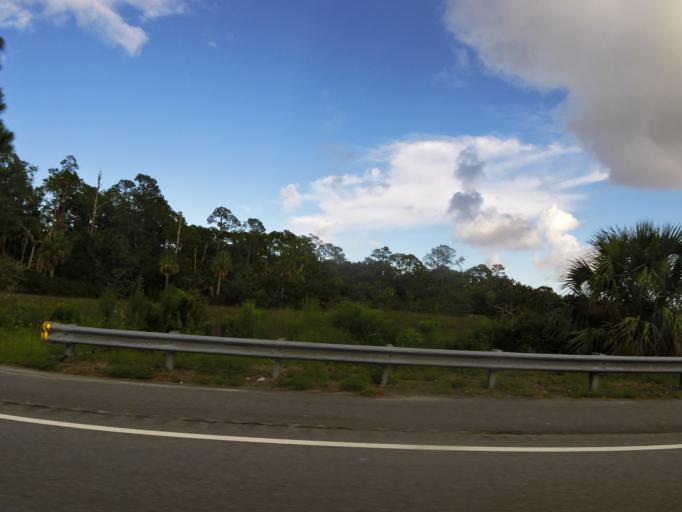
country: US
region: Georgia
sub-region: Glynn County
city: Country Club Estates
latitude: 31.1962
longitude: -81.4685
